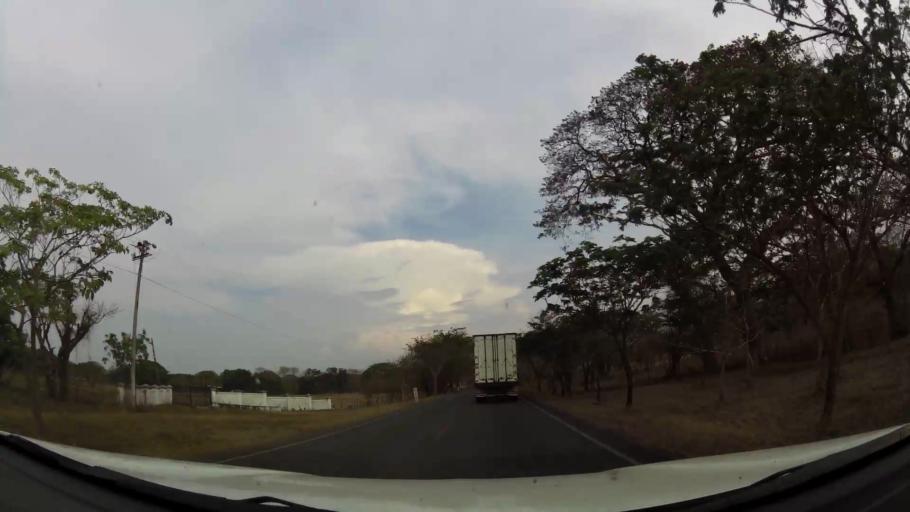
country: NI
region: Rivas
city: Cardenas
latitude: 11.2706
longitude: -85.6502
